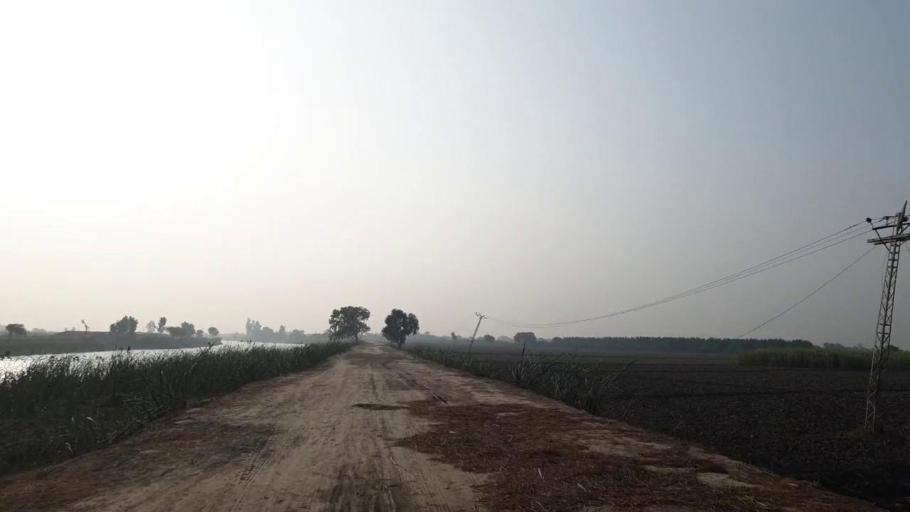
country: PK
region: Sindh
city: Tando Muhammad Khan
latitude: 25.0965
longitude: 68.5768
